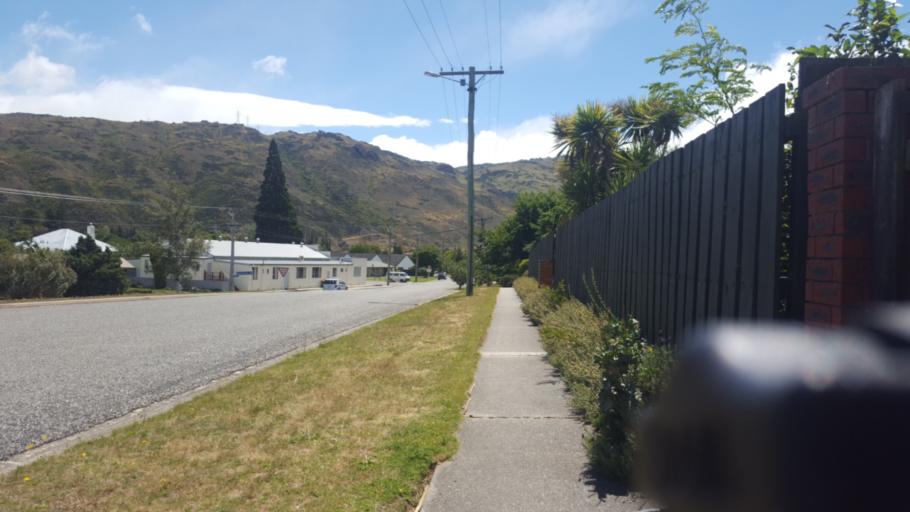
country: NZ
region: Otago
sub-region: Queenstown-Lakes District
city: Wanaka
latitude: -45.1885
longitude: 169.3214
